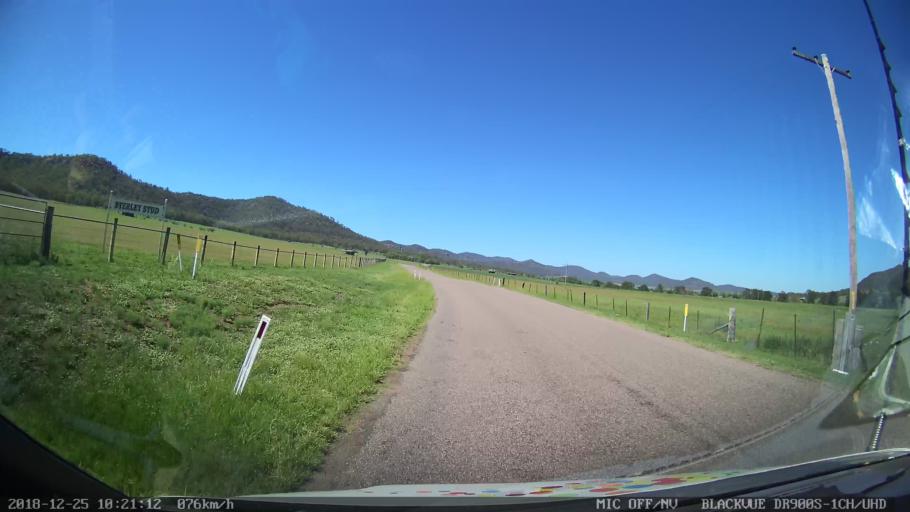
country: AU
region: New South Wales
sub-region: Muswellbrook
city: Denman
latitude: -32.3648
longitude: 150.5425
